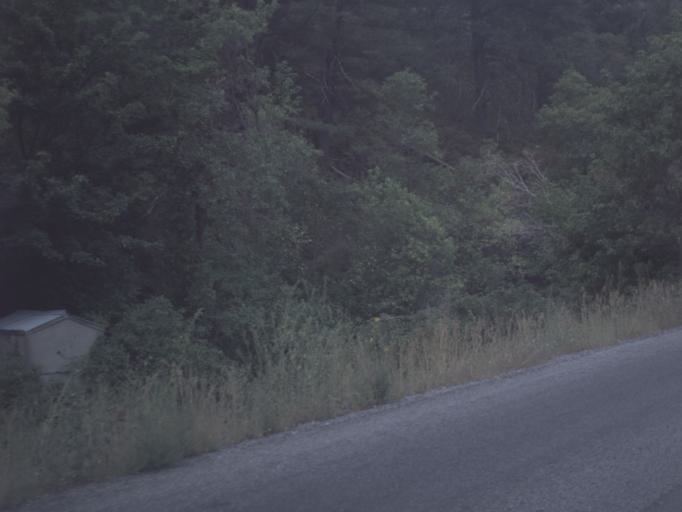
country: US
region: Utah
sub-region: Utah County
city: Orem
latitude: 40.3686
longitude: -111.5616
